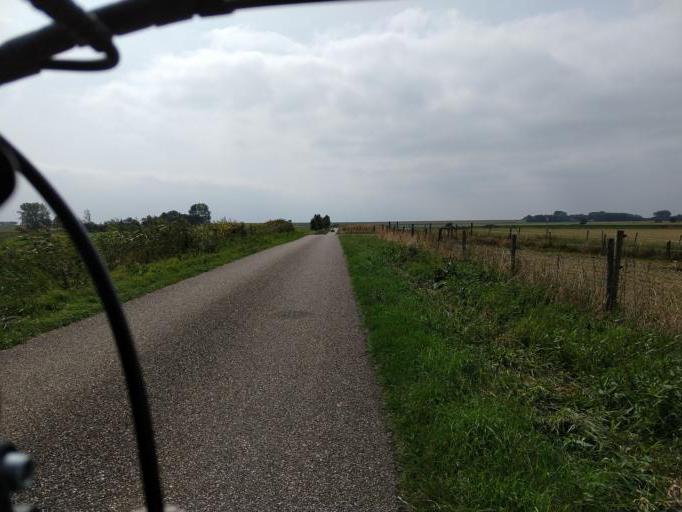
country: NL
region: Zeeland
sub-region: Schouwen-Duiveland
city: Bruinisse
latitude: 51.6257
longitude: 4.0094
